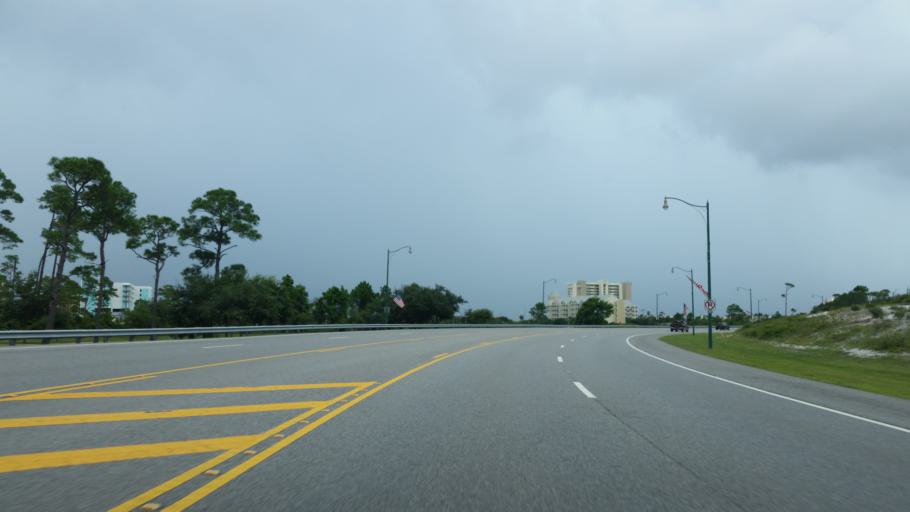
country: US
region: Alabama
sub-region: Baldwin County
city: Orange Beach
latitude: 30.2752
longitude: -87.5811
